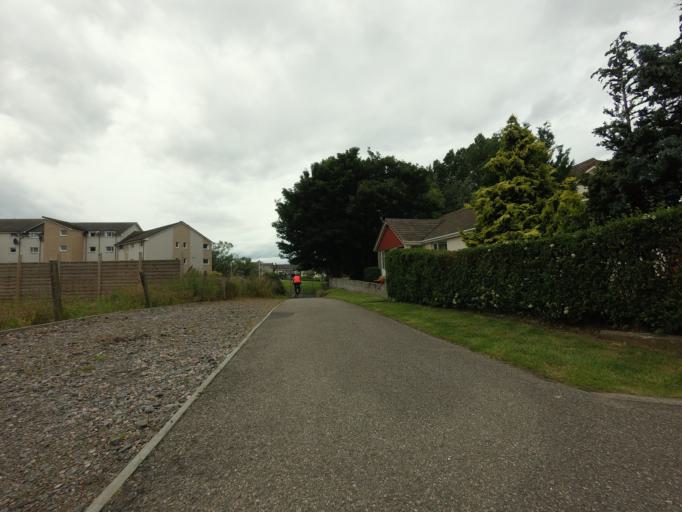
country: GB
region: Scotland
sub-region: Highland
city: Nairn
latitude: 57.5860
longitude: -3.8618
